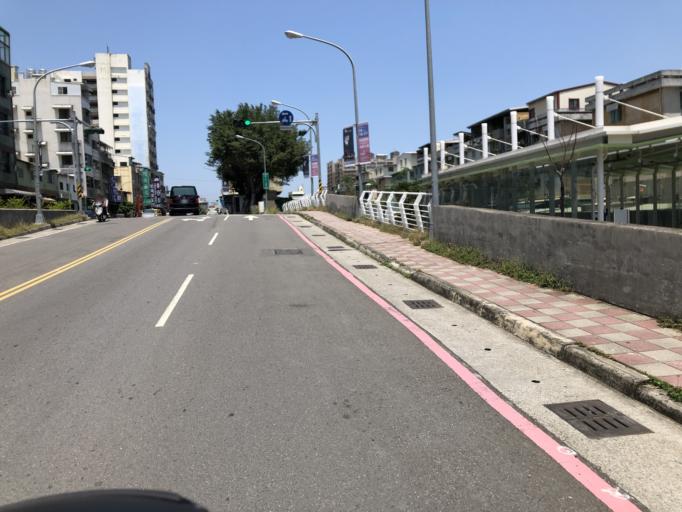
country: TW
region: Kaohsiung
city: Kaohsiung
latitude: 22.6295
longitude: 120.2805
